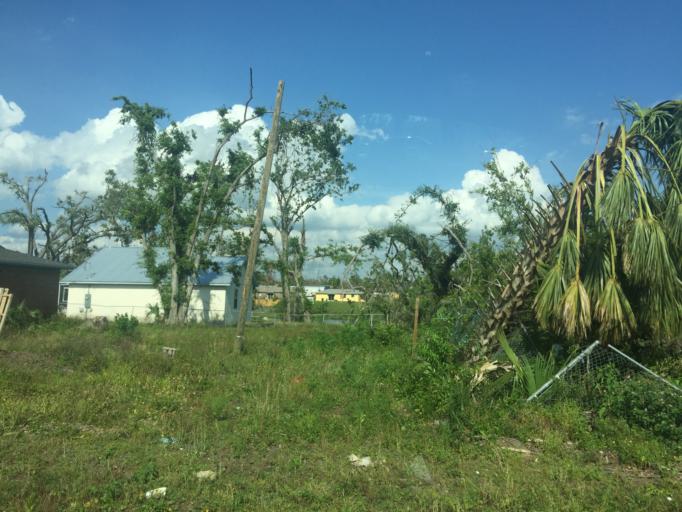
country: US
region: Florida
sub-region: Bay County
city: Springfield
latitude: 30.1624
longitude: -85.6036
